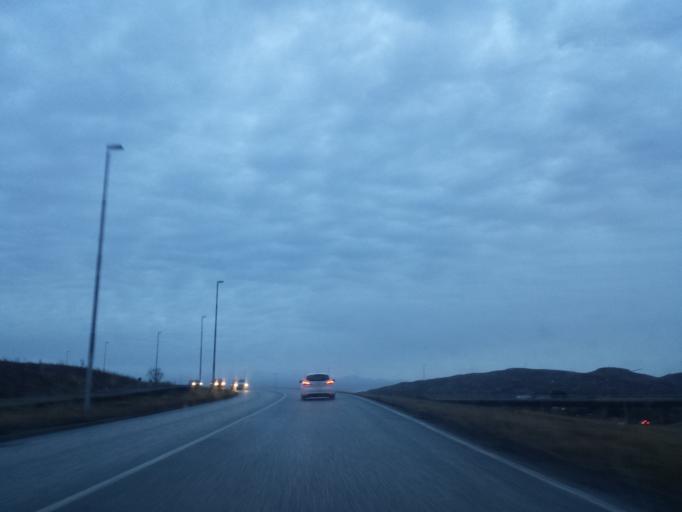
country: IS
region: Capital Region
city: Mosfellsbaer
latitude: 64.1317
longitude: -21.7672
